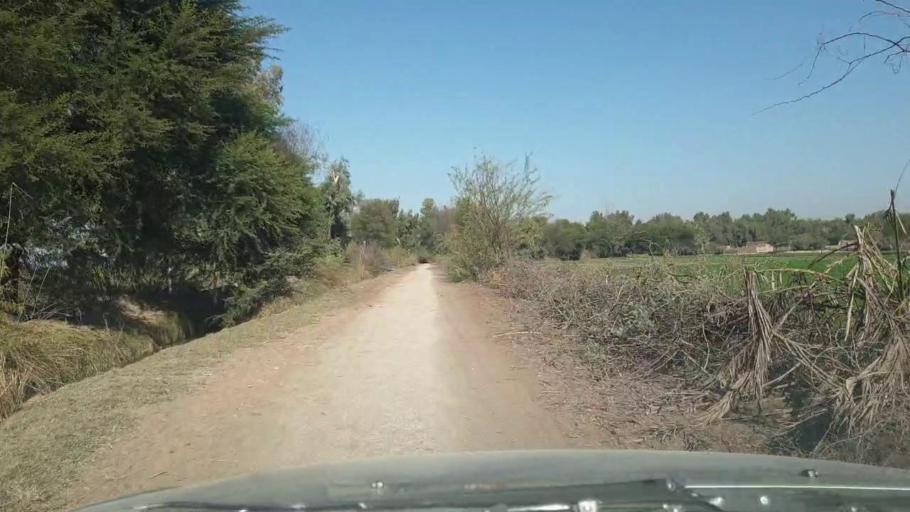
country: PK
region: Sindh
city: Adilpur
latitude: 27.8972
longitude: 69.2548
